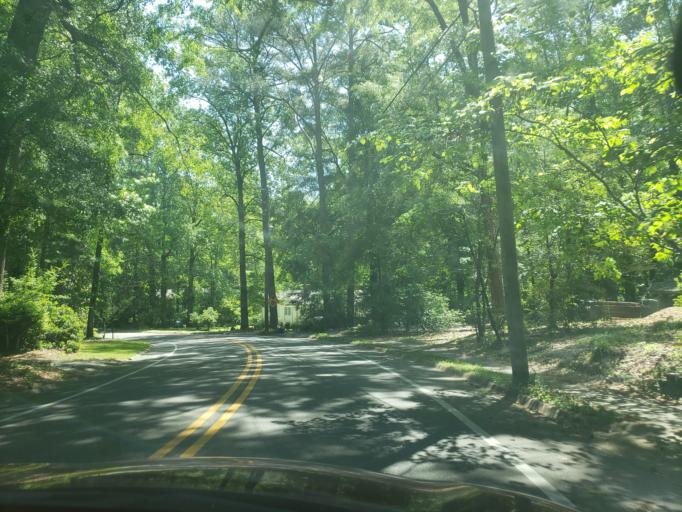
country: US
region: Alabama
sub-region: Lee County
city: Auburn
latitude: 32.5884
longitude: -85.4803
